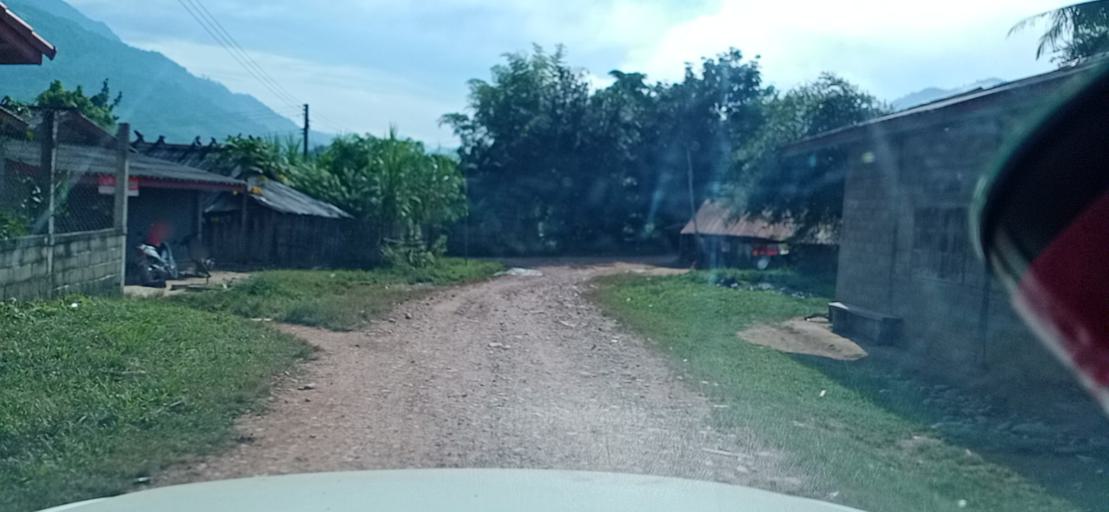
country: TH
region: Changwat Bueng Kan
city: Pak Khat
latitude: 18.6763
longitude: 103.1942
